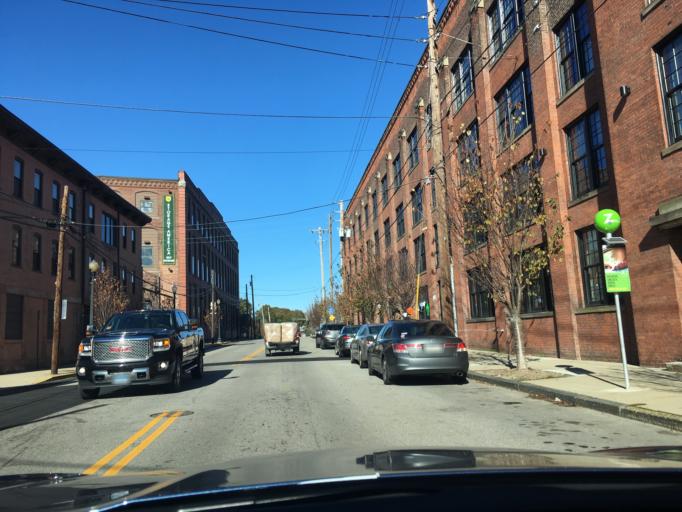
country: US
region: Rhode Island
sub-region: Providence County
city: Pawtucket
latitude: 41.8865
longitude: -71.3822
